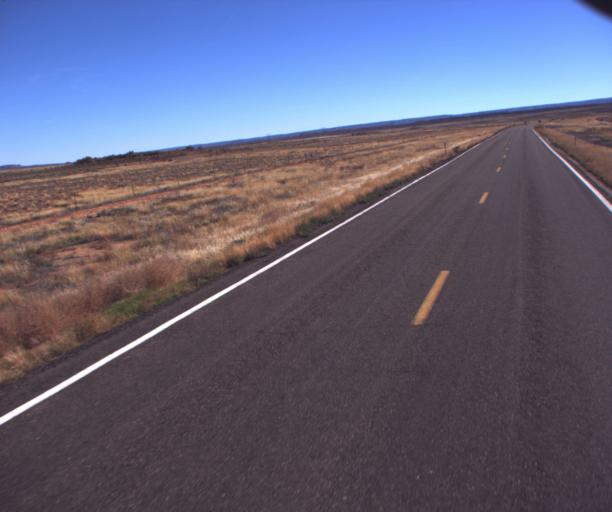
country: US
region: Arizona
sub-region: Coconino County
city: Fredonia
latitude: 36.9222
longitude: -112.4448
